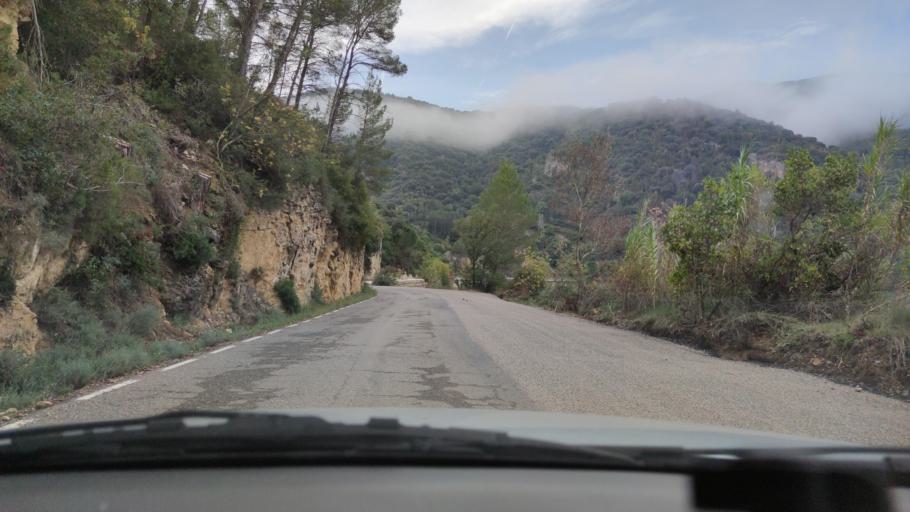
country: ES
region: Catalonia
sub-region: Provincia de Lleida
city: Llimiana
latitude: 42.0585
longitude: 0.8890
